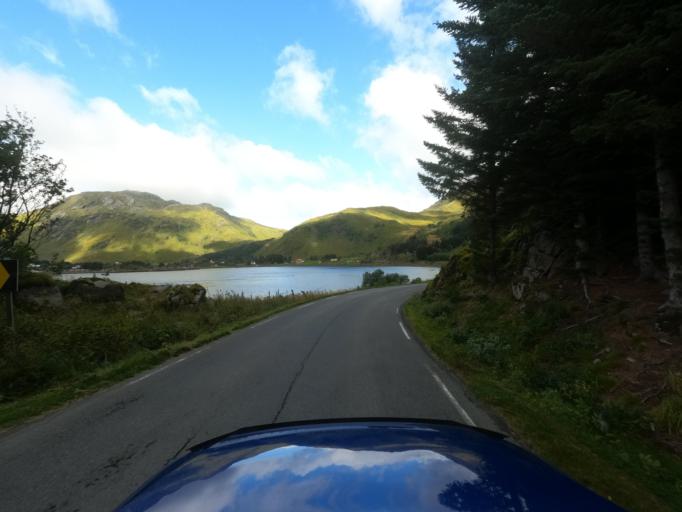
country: NO
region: Nordland
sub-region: Vestvagoy
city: Evjen
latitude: 68.1983
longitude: 13.8951
